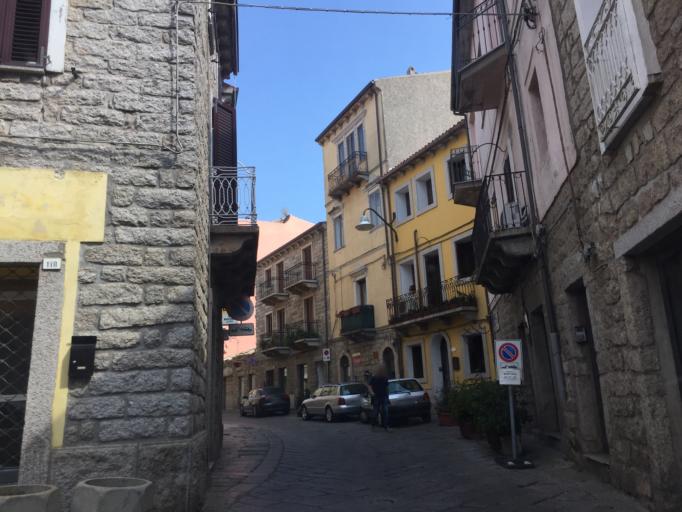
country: IT
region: Sardinia
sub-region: Provincia di Olbia-Tempio
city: Tempio Pausania
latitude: 40.9039
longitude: 9.1026
